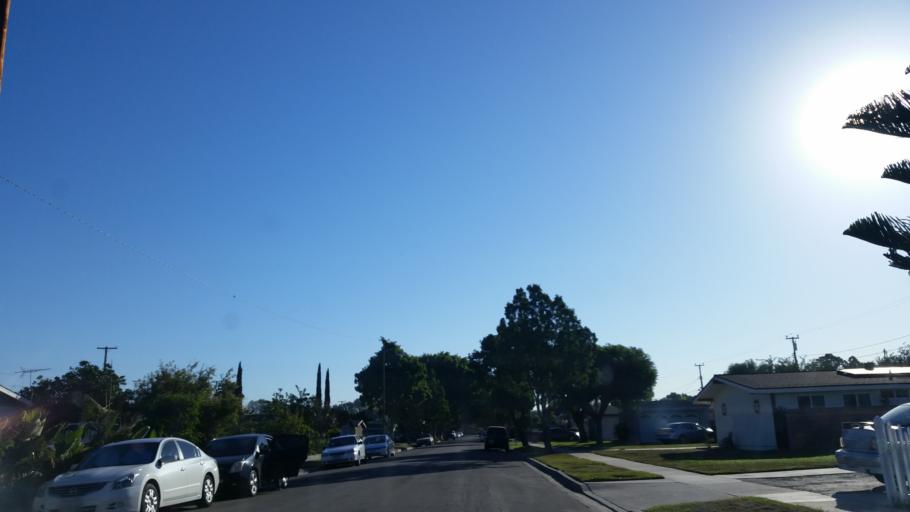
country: US
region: California
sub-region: Los Angeles County
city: Lakewood
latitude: 33.8651
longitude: -118.1554
